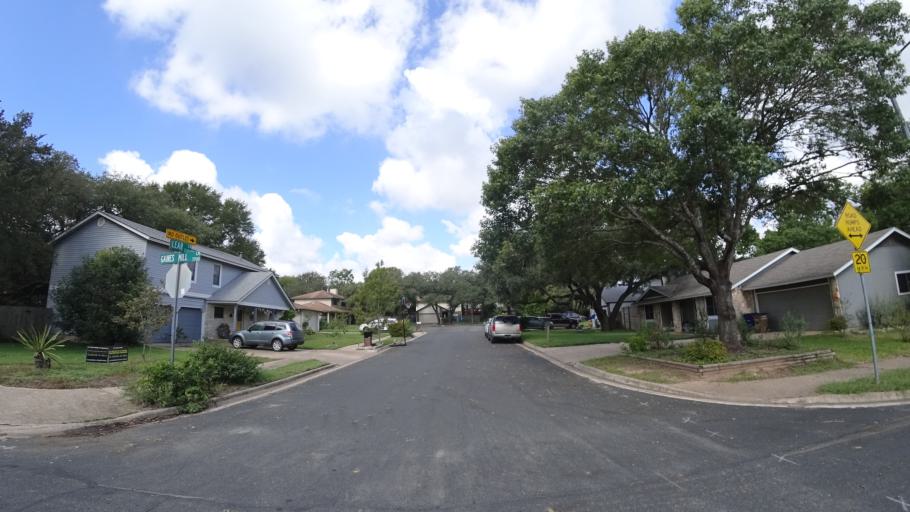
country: US
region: Texas
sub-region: Travis County
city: Shady Hollow
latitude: 30.1976
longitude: -97.8146
